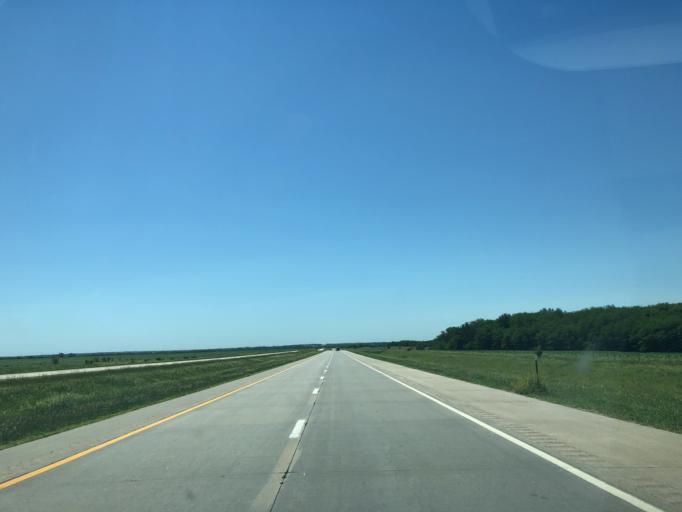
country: US
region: Kansas
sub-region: Cloud County
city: Concordia
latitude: 39.6344
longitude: -97.6604
